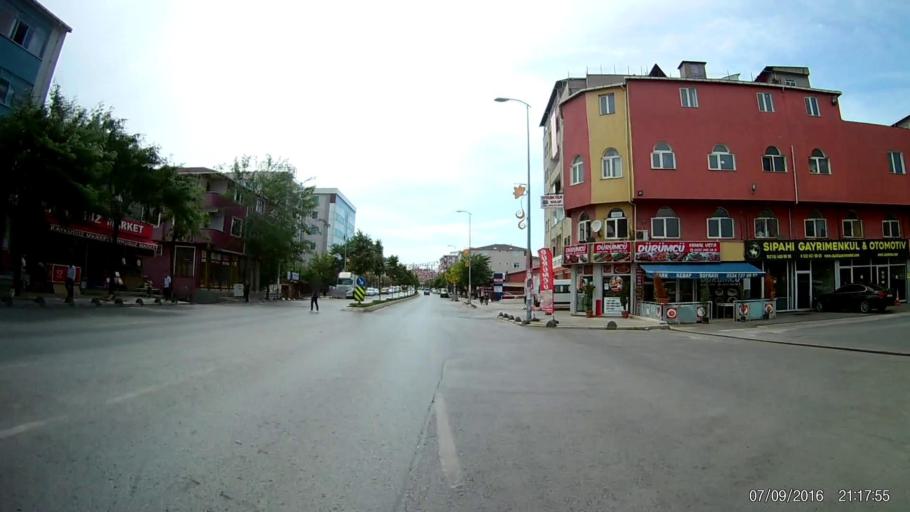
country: TR
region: Istanbul
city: Sultanbeyli
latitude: 40.9643
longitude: 29.2806
